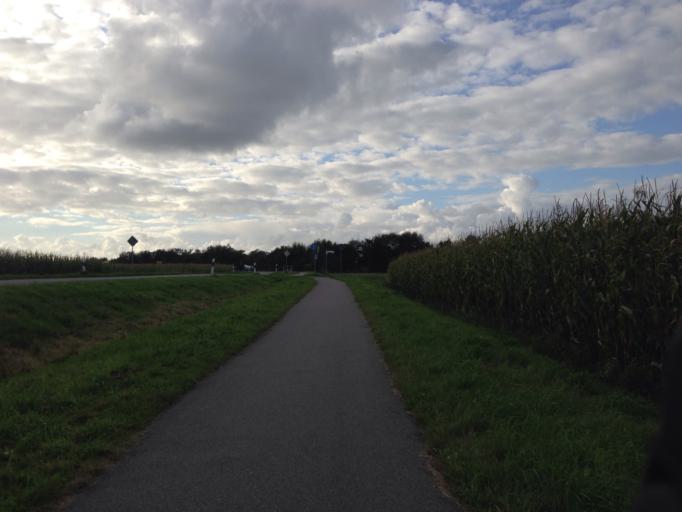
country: DE
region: Schleswig-Holstein
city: Oldsum
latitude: 54.7288
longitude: 8.4477
